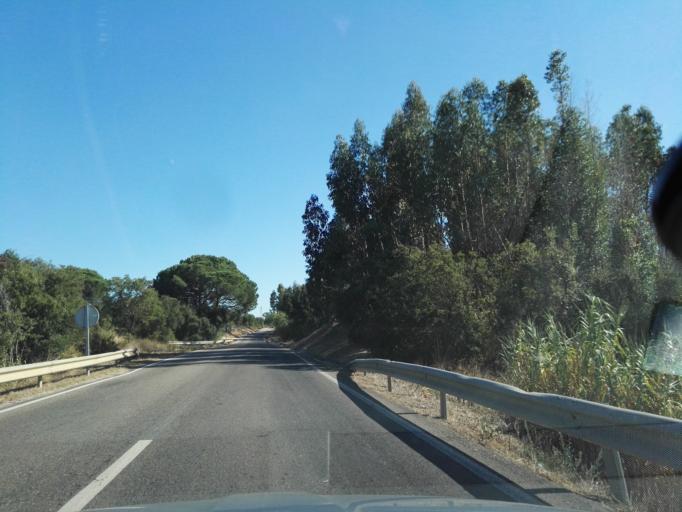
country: PT
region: Santarem
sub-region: Benavente
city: Benavente
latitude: 38.9355
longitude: -8.7827
